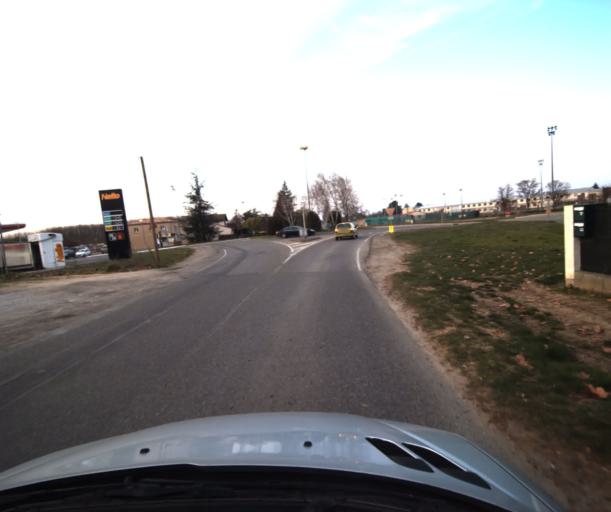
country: FR
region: Midi-Pyrenees
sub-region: Departement du Tarn-et-Garonne
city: Labastide-Saint-Pierre
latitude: 43.9125
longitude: 1.3688
